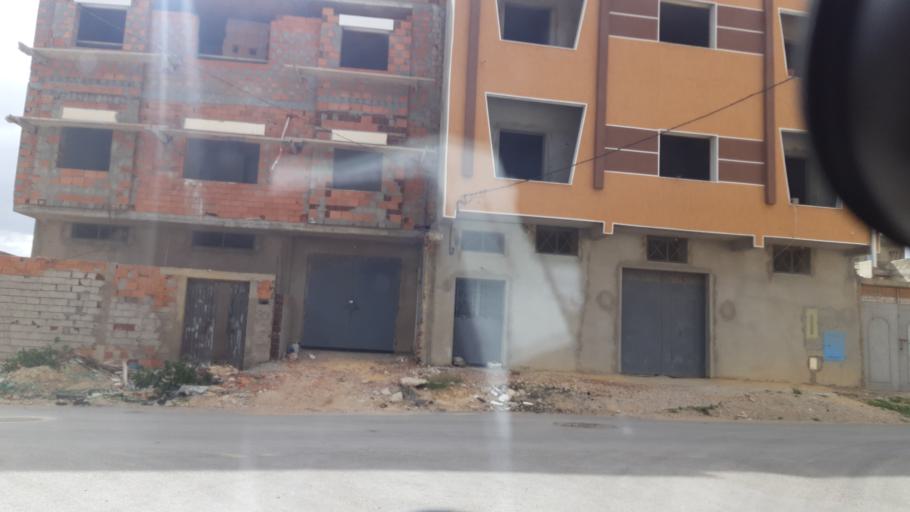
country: TN
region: Susah
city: Akouda
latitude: 35.8695
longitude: 10.5197
